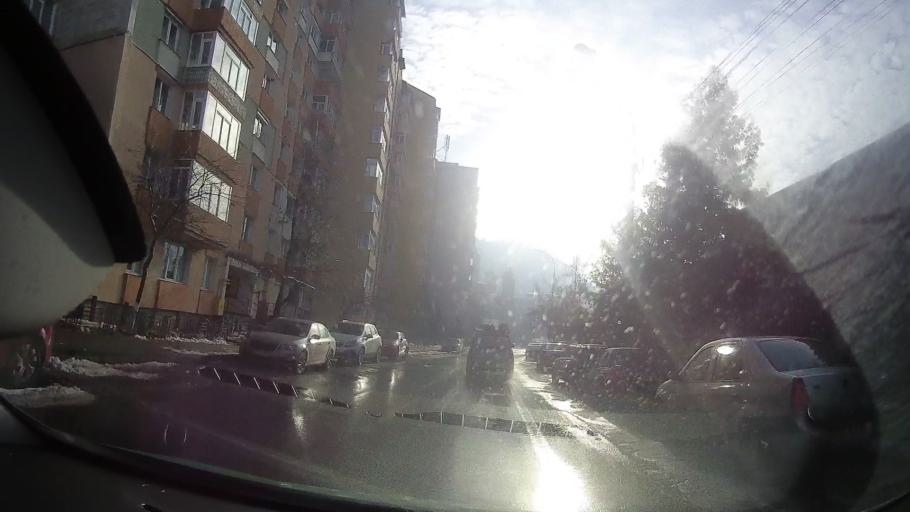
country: RO
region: Neamt
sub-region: Municipiul Piatra-Neamt
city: Valeni
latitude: 46.9386
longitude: 26.3811
